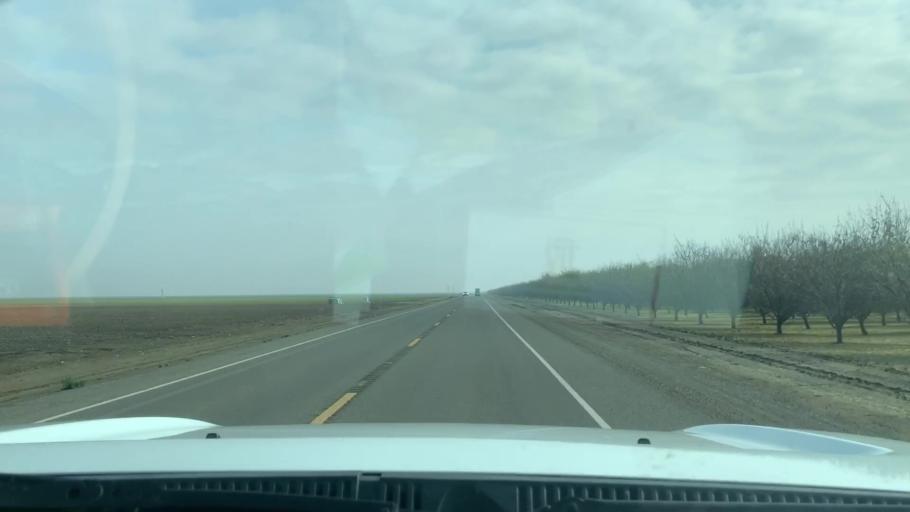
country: US
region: California
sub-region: Fresno County
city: Huron
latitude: 36.2554
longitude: -120.0413
